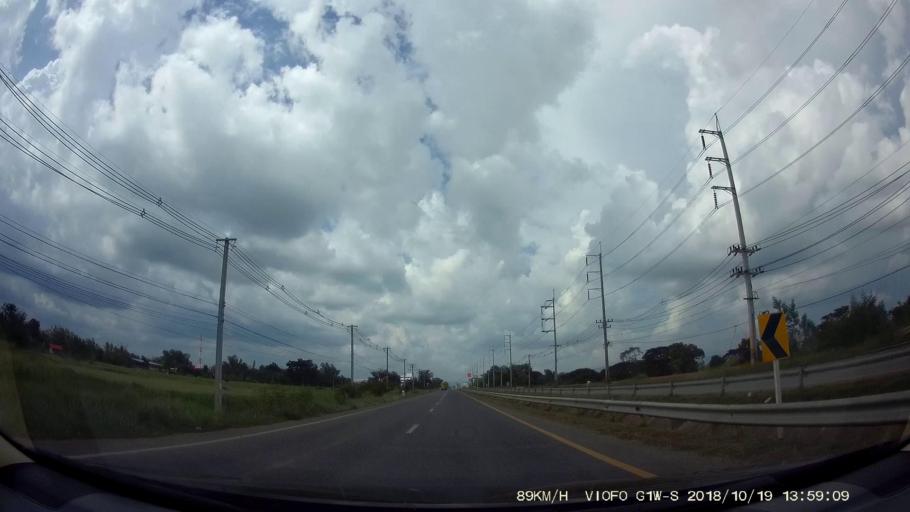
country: TH
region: Chaiyaphum
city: Chaiyaphum
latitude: 15.8055
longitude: 102.0613
